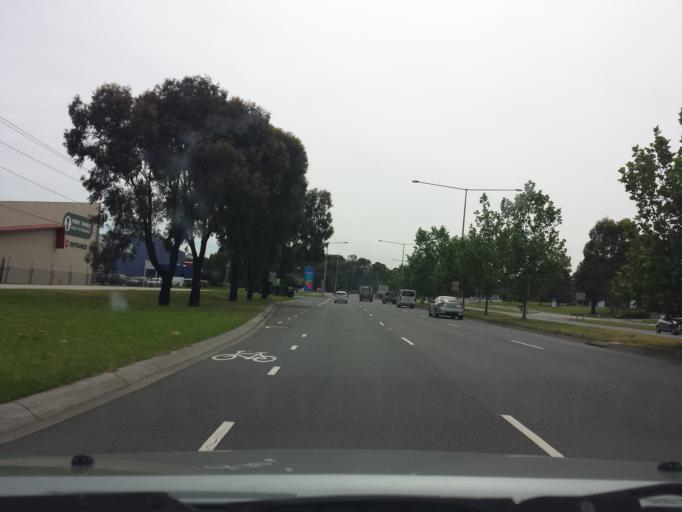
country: AU
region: Victoria
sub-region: Knox
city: Scoresby
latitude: -37.9003
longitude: 145.2198
